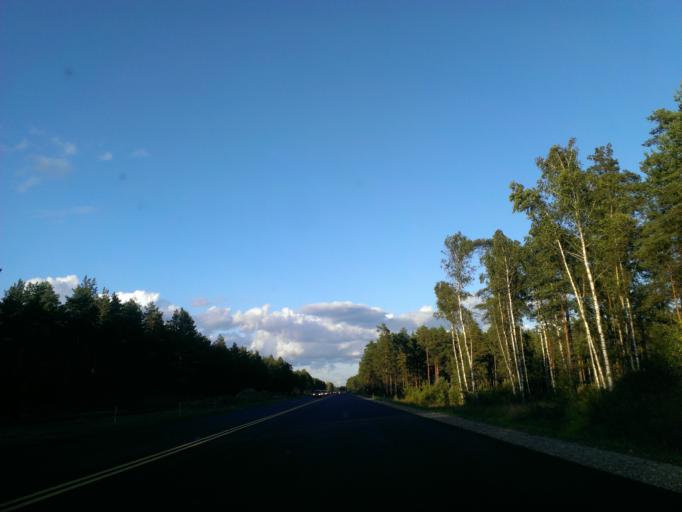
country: LV
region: Garkalne
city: Garkalne
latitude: 57.0313
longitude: 24.3743
